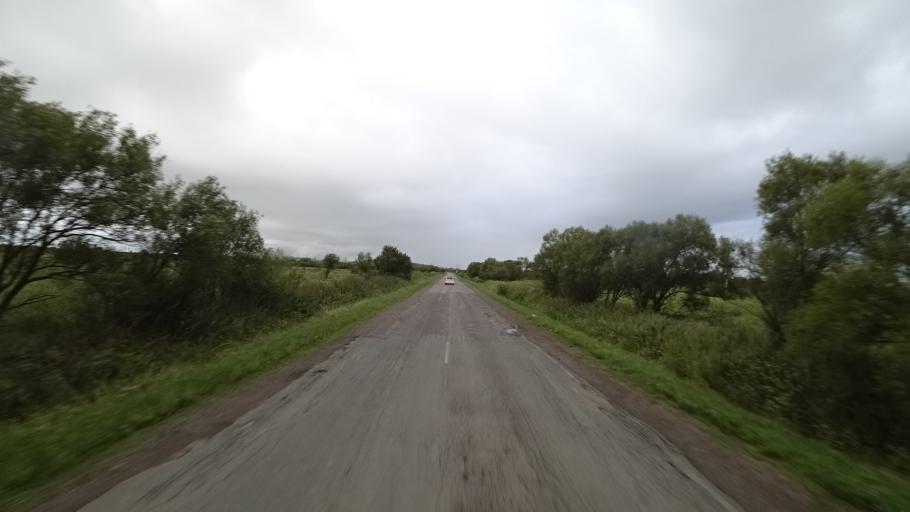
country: RU
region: Primorskiy
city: Chernigovka
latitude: 44.3602
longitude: 132.5564
